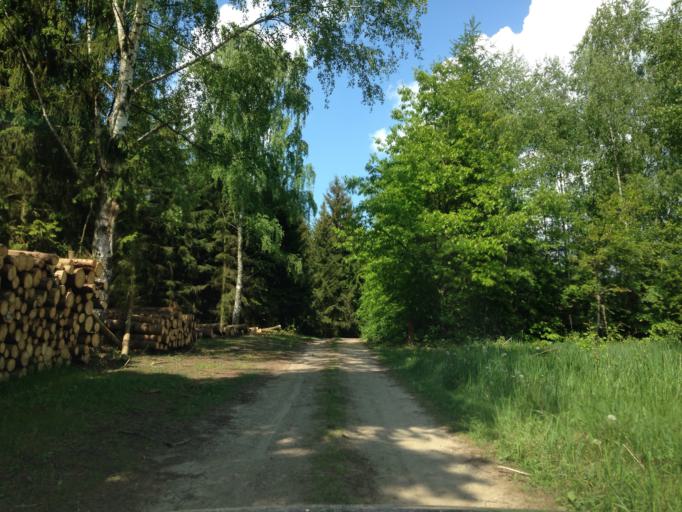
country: PL
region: Kujawsko-Pomorskie
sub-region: Powiat brodnicki
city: Brodnica
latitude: 53.3231
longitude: 19.3658
